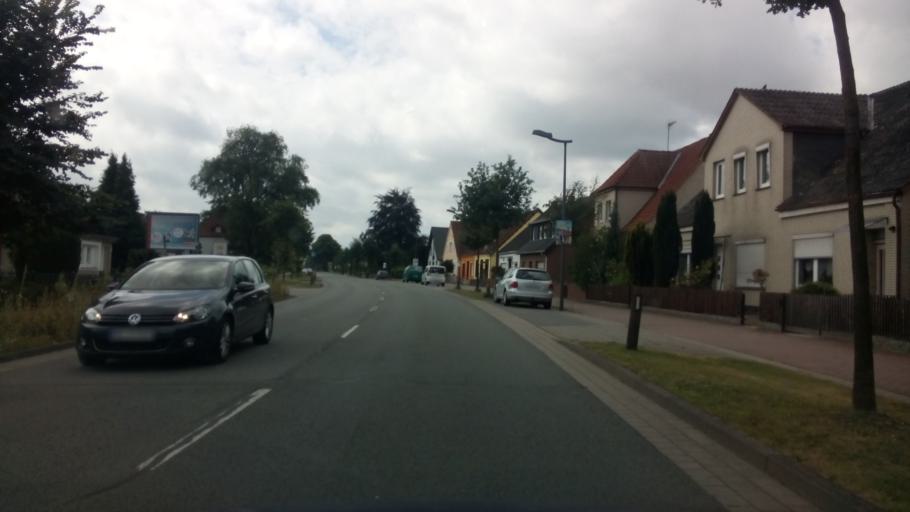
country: DE
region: Lower Saxony
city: Barnstorf
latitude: 52.7084
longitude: 8.4978
